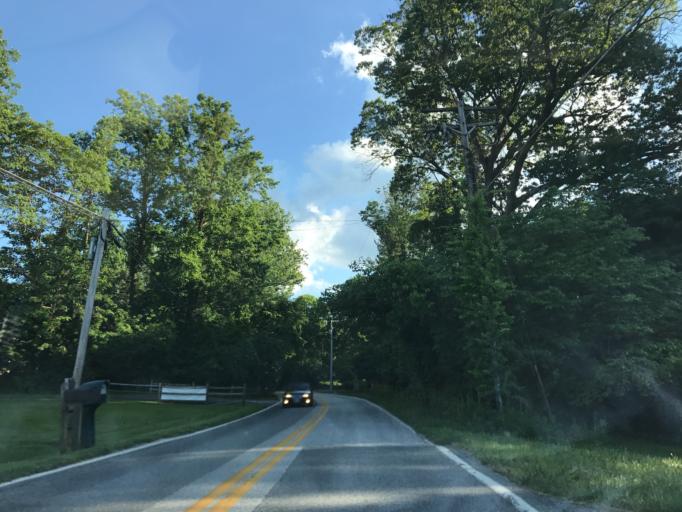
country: US
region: Maryland
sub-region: Baltimore County
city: Hunt Valley
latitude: 39.5261
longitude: -76.5718
